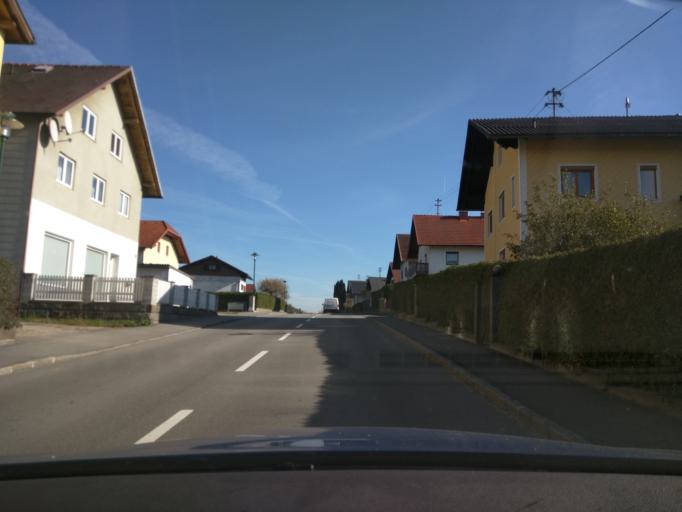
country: DE
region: Bavaria
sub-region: Lower Bavaria
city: Obernzell
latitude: 48.5426
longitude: 13.5786
